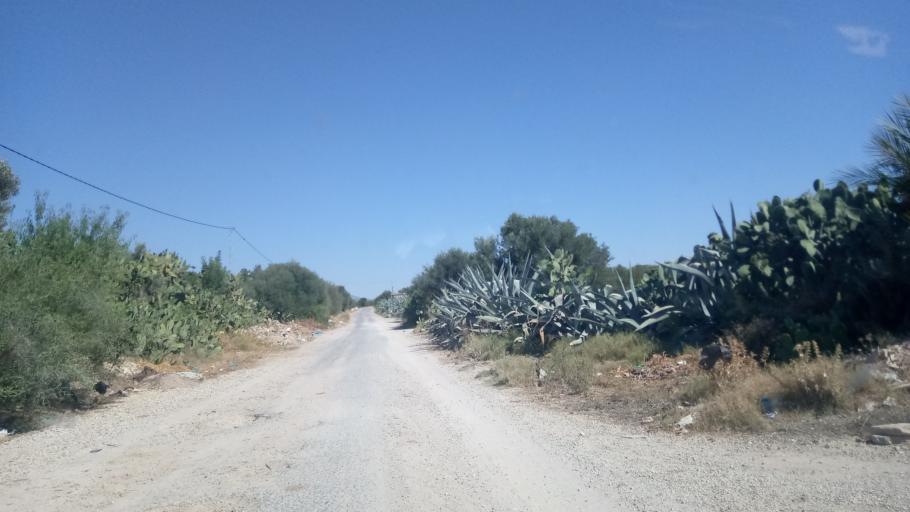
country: TN
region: Al Qayrawan
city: Sbikha
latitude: 36.1267
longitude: 10.0857
